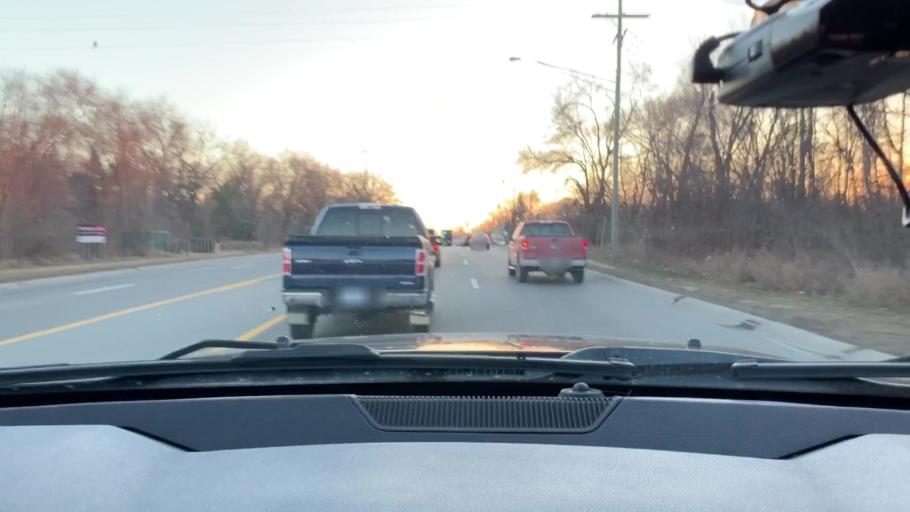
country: US
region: Michigan
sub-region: Wayne County
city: Woodhaven
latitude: 42.1338
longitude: -83.2693
